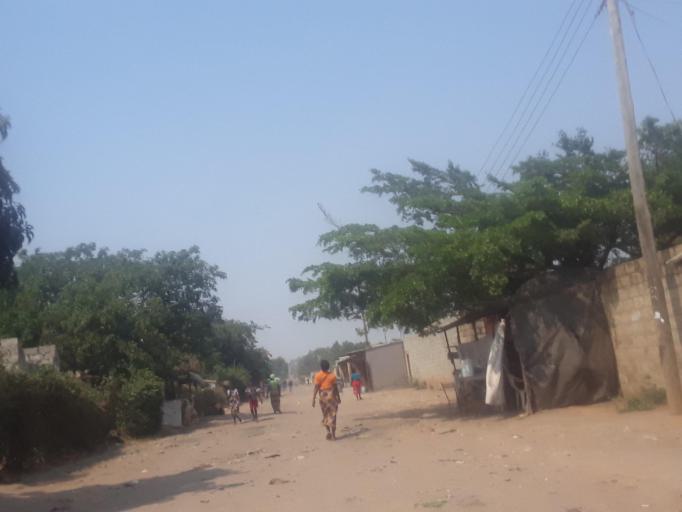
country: ZM
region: Lusaka
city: Lusaka
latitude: -15.3522
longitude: 28.2880
